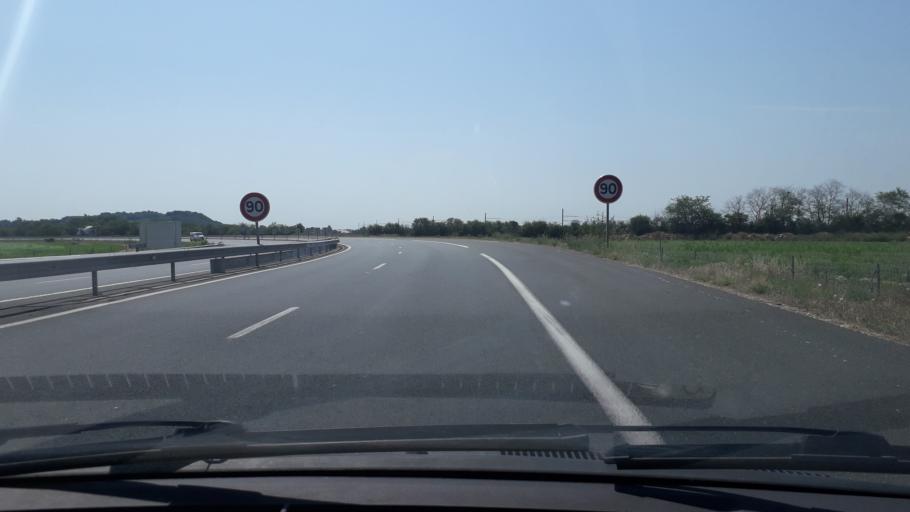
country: FR
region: Rhone-Alpes
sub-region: Departement du Rhone
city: Jonage
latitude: 45.7682
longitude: 5.0404
